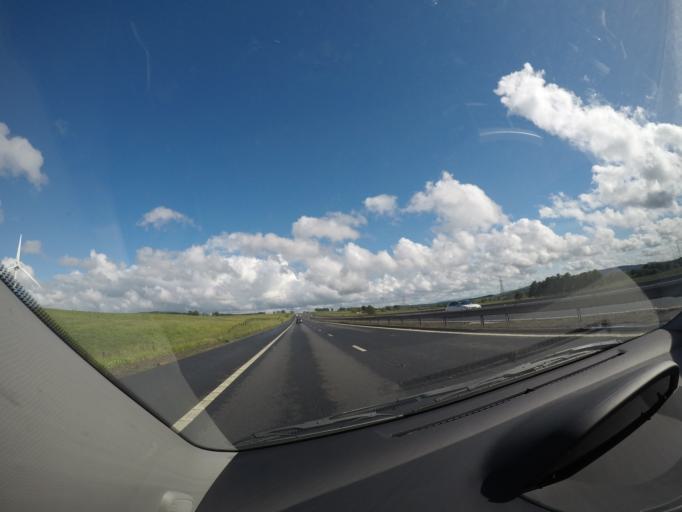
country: GB
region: Scotland
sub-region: South Lanarkshire
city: Lesmahagow
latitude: 55.6211
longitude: -3.8546
